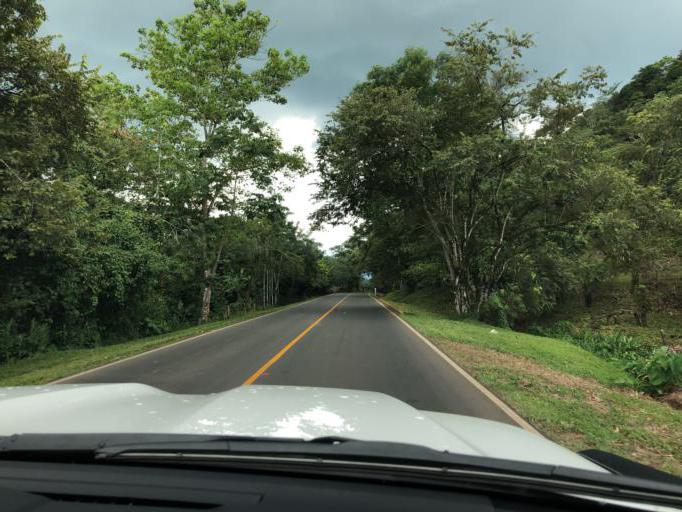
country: NI
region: Chontales
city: Villa Sandino
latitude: 11.9964
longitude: -84.8304
